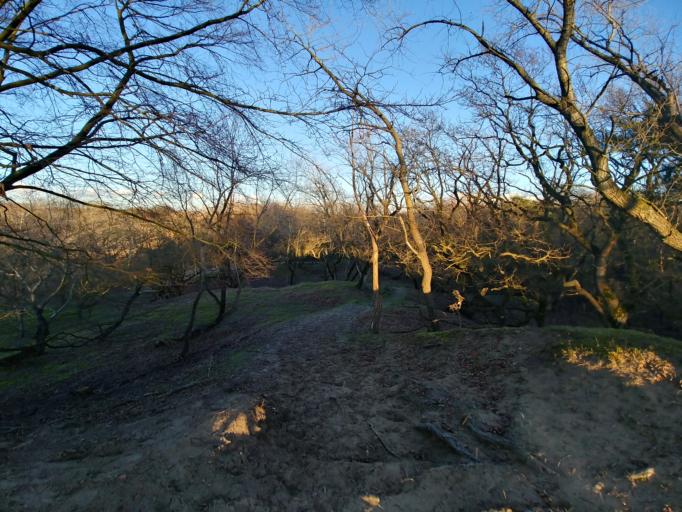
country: NL
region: North Holland
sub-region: Gemeente Bloemendaal
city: Bennebroek
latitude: 52.3318
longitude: 4.5620
